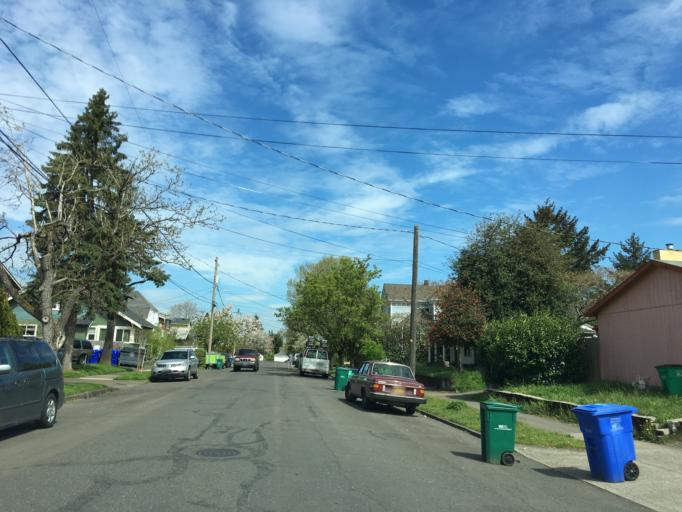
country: US
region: Oregon
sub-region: Multnomah County
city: Lents
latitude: 45.5267
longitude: -122.5814
